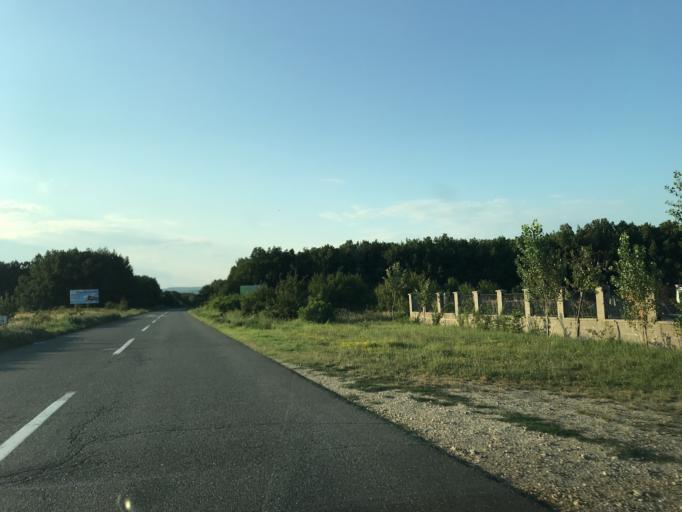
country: RO
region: Mehedinti
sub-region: Comuna Gogosu
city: Ostrovu Mare
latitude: 44.4409
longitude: 22.4568
